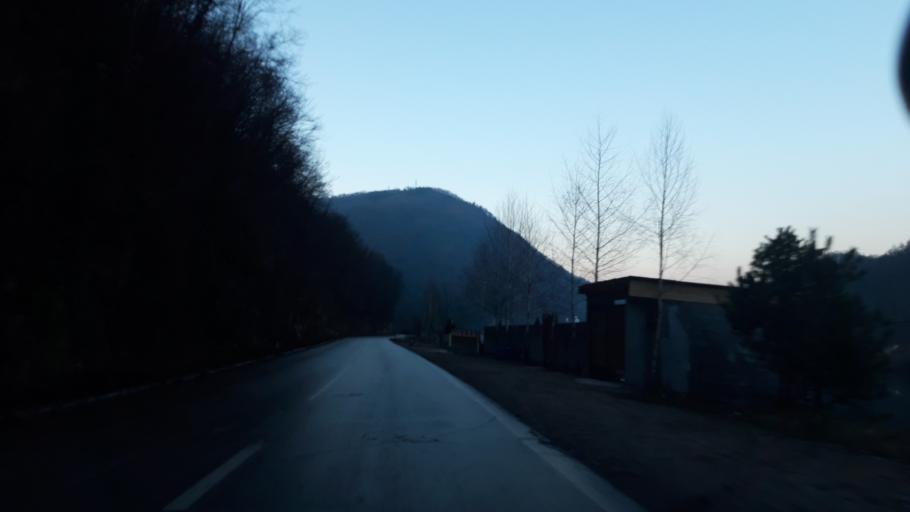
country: RS
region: Central Serbia
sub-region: Macvanski Okrug
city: Mali Zvornik
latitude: 44.3478
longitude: 19.1114
